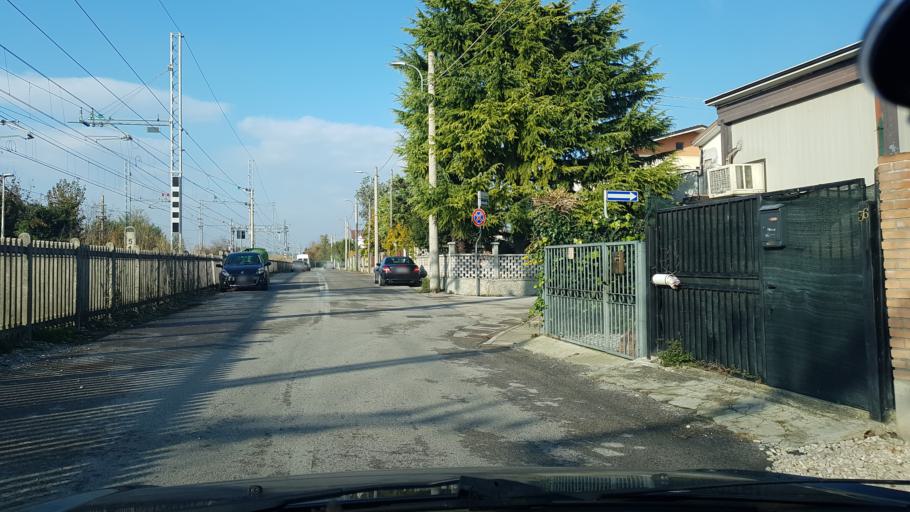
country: IT
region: Friuli Venezia Giulia
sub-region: Provincia di Gorizia
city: Ronchi dei Legionari
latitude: 45.8319
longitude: 13.5045
